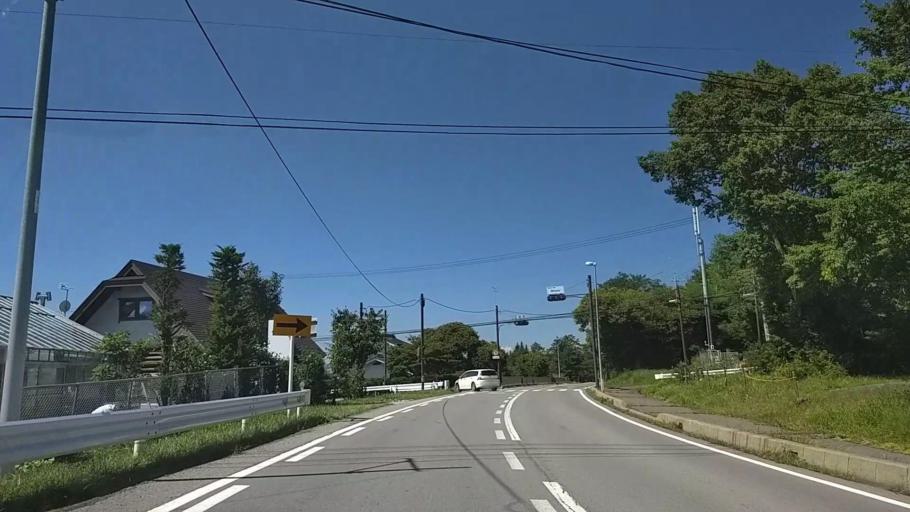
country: JP
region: Nagano
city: Komoro
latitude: 36.3353
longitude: 138.5135
